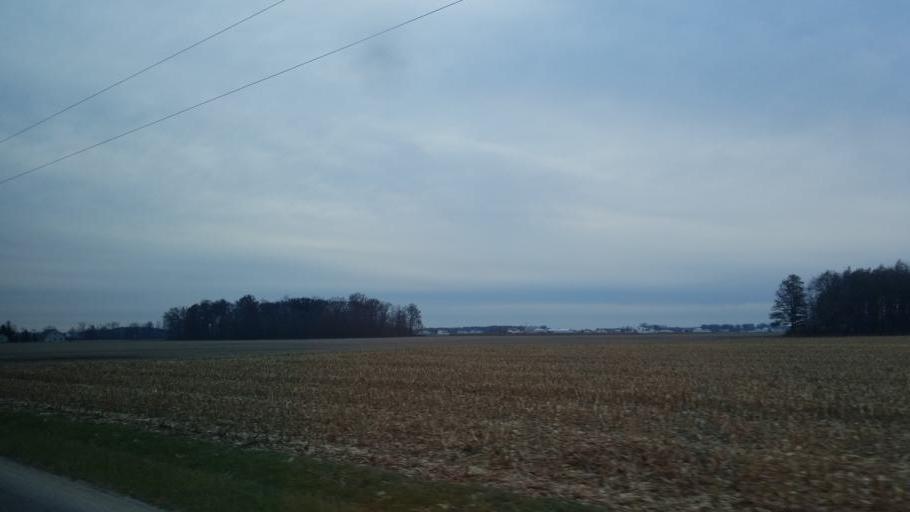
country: US
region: Indiana
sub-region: Adams County
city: Berne
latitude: 40.7276
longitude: -84.8796
